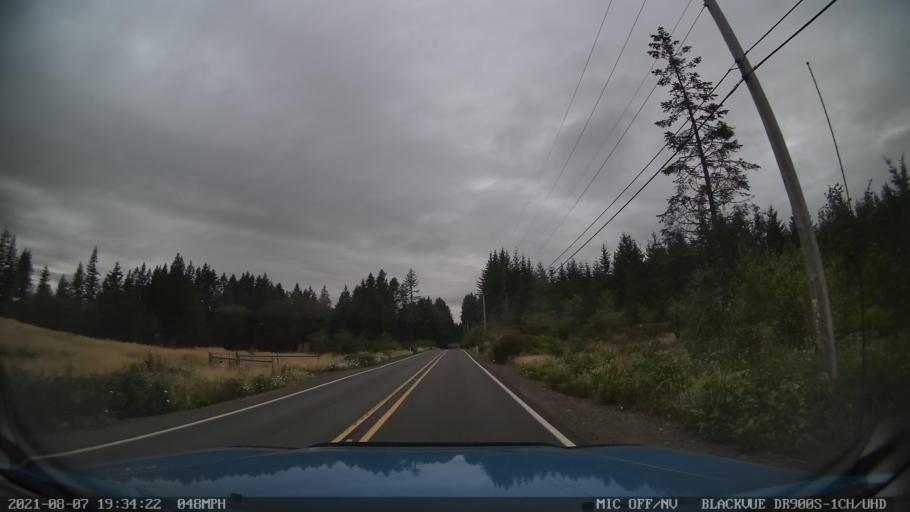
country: US
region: Oregon
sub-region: Linn County
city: Lyons
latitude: 44.9167
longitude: -122.6551
